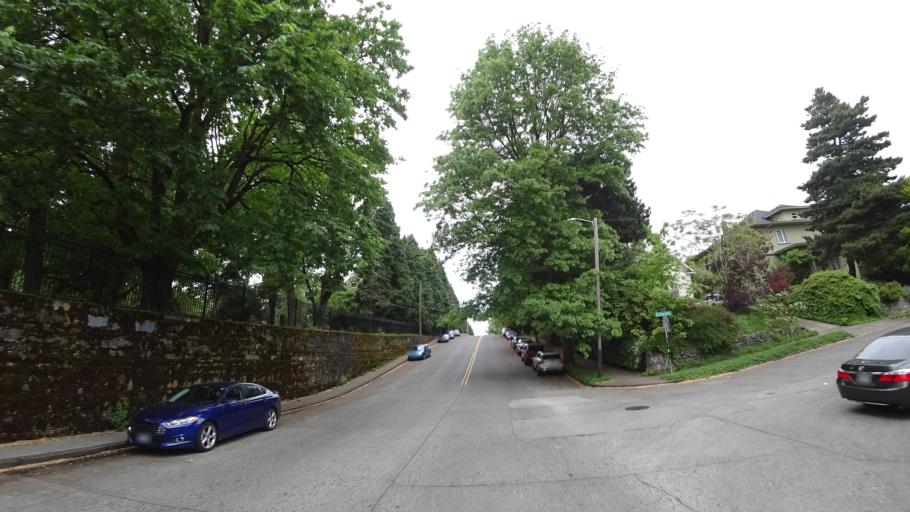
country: US
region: Oregon
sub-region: Multnomah County
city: Portland
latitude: 45.5170
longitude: -122.6391
